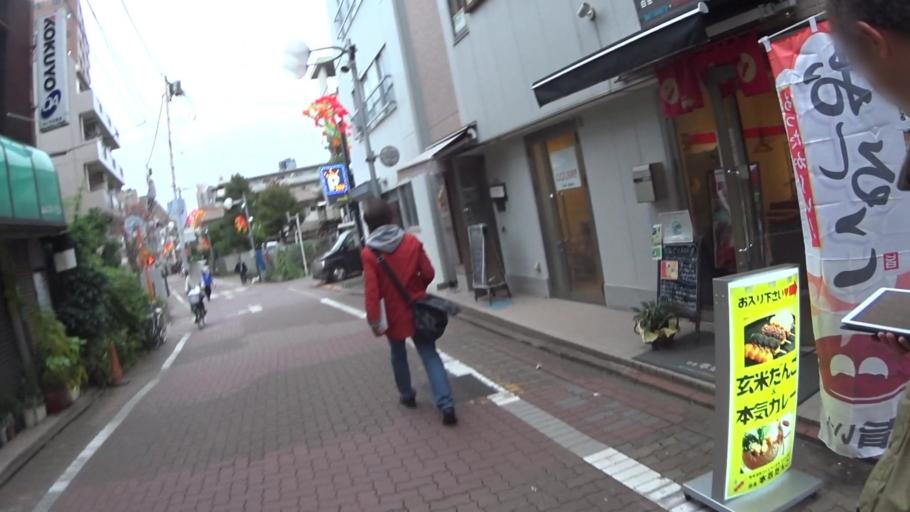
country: JP
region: Tokyo
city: Tokyo
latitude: 35.6445
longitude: 139.7315
